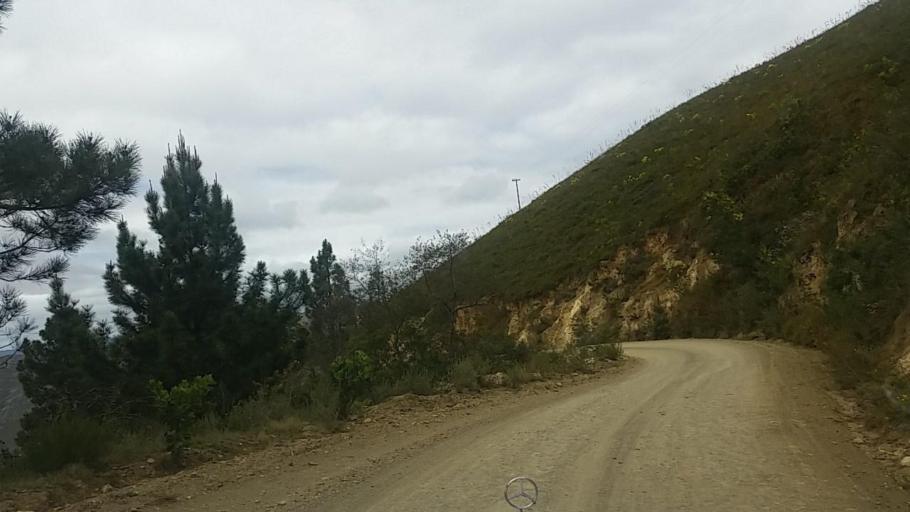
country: ZA
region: Western Cape
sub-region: Eden District Municipality
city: Knysna
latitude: -33.7570
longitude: 23.1564
